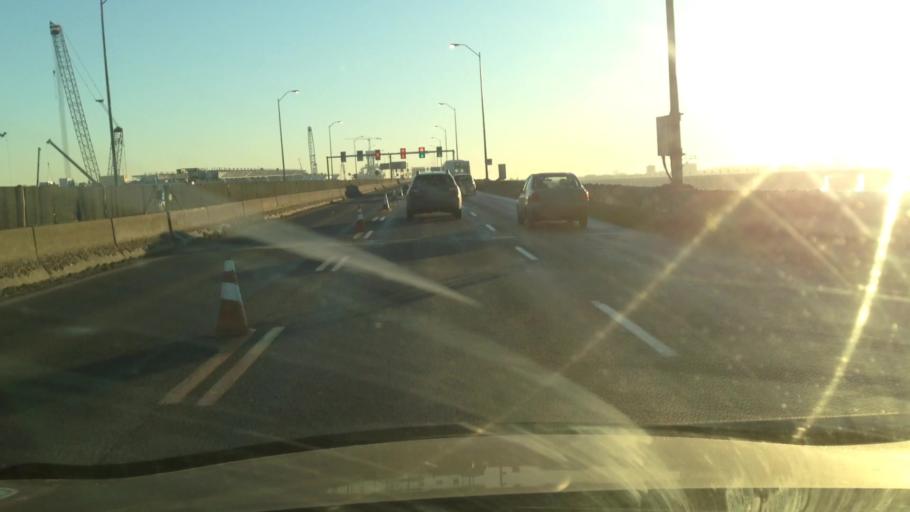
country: CA
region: Quebec
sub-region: Monteregie
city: La Prairie
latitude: 45.4695
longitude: -73.5319
